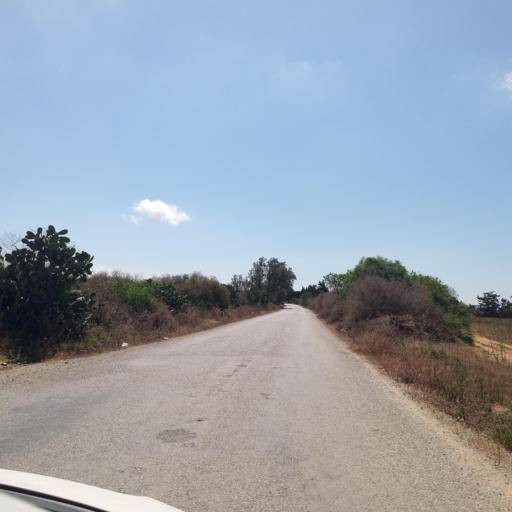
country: TN
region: Nabul
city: Qulaybiyah
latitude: 36.8617
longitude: 11.0409
